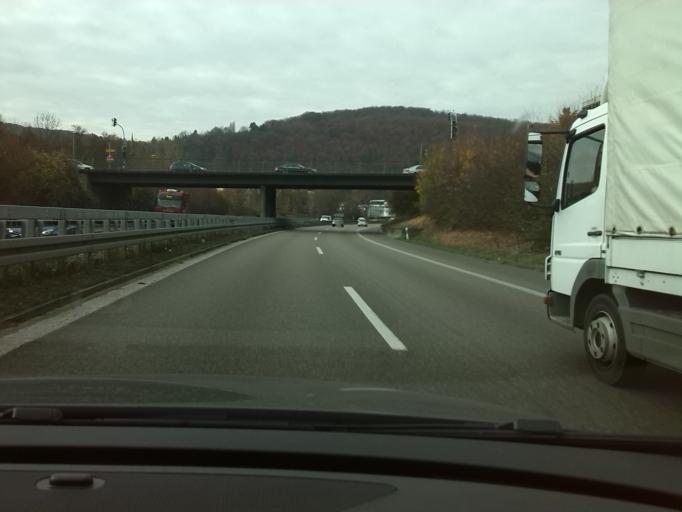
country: DE
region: Baden-Wuerttemberg
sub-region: Regierungsbezirk Stuttgart
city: Esslingen
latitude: 48.7405
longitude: 9.2763
